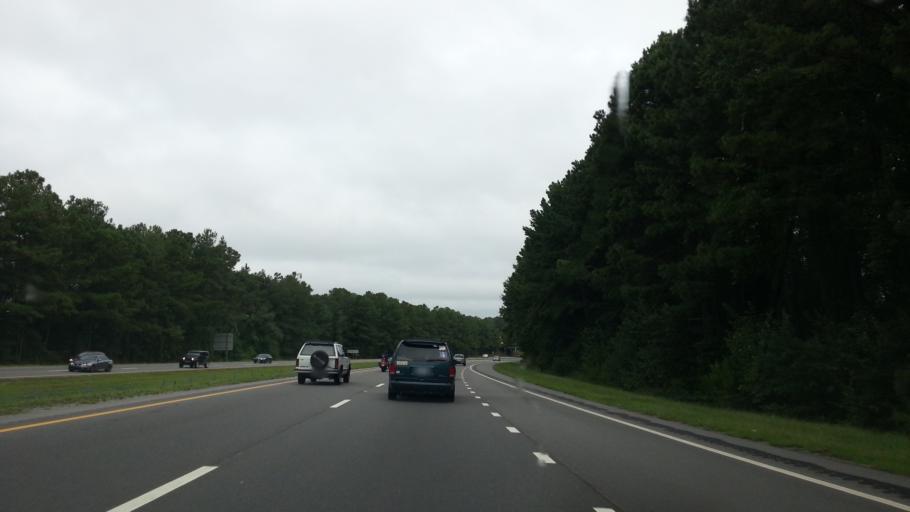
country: US
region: North Carolina
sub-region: Cumberland County
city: Fort Bragg
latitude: 35.0785
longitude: -78.9618
